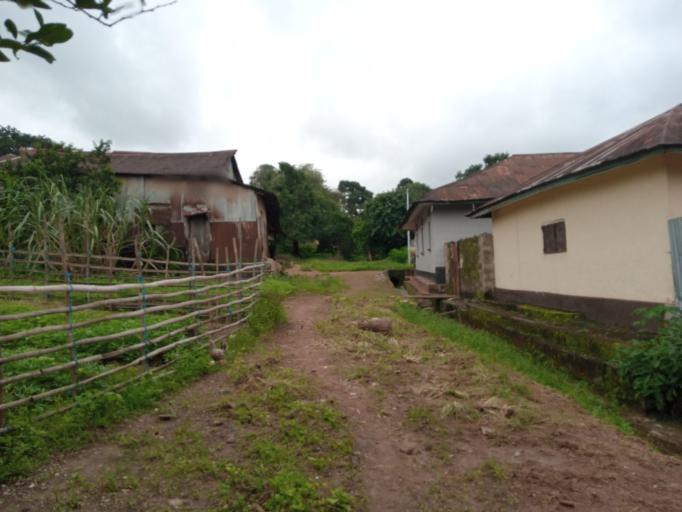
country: SL
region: Southern Province
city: Largo
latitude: 8.2048
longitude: -12.0598
